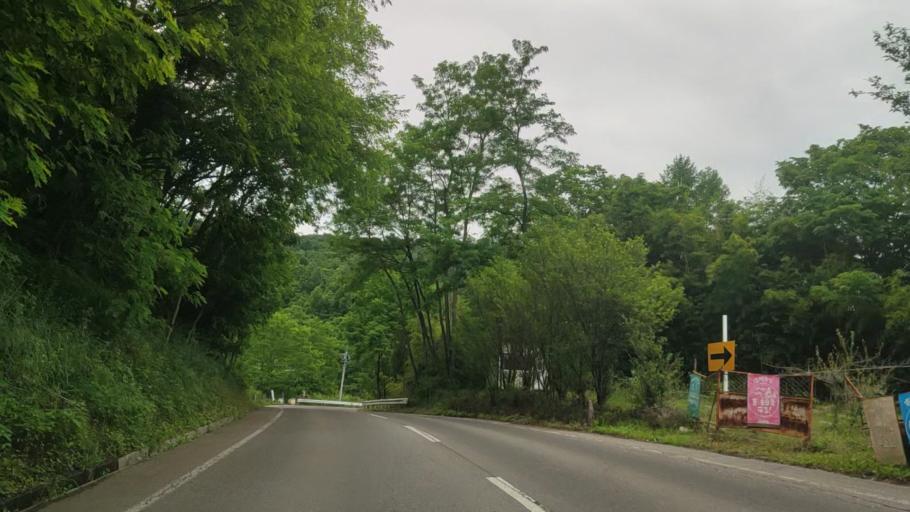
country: JP
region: Nagano
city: Kamimaruko
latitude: 36.3160
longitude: 138.3323
